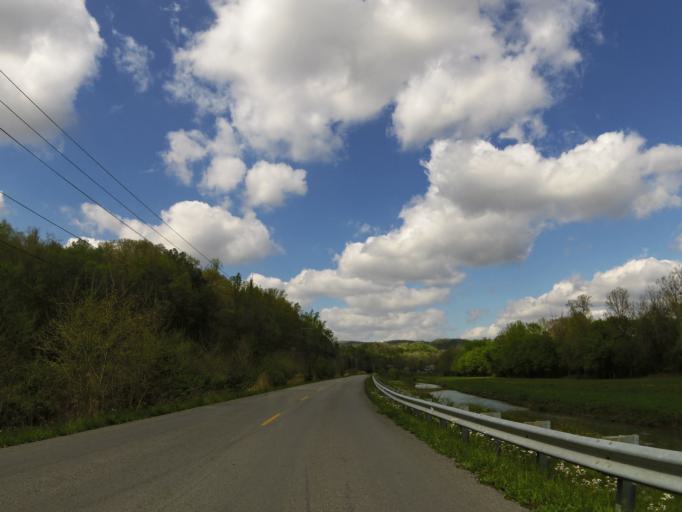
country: US
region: Kentucky
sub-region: Bell County
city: Middlesboro
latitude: 36.6226
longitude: -83.7364
